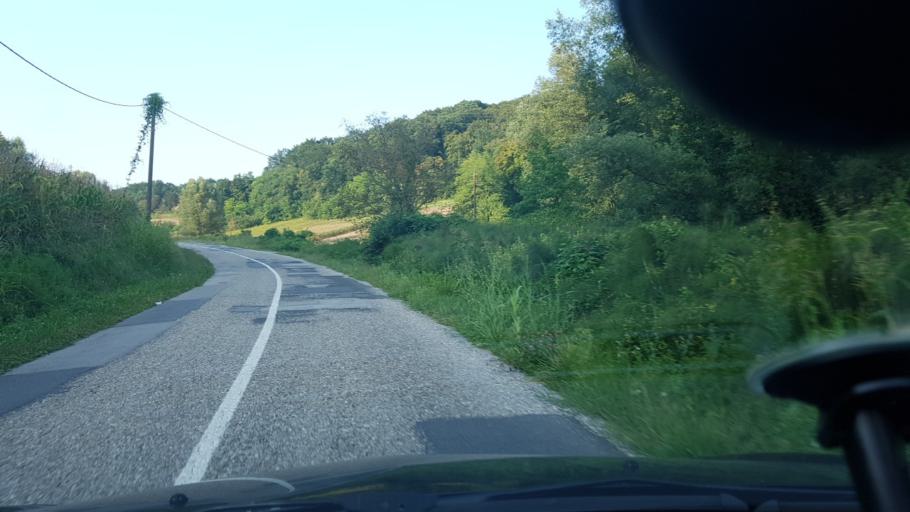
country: HR
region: Krapinsko-Zagorska
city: Zabok
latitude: 46.0356
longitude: 15.8586
